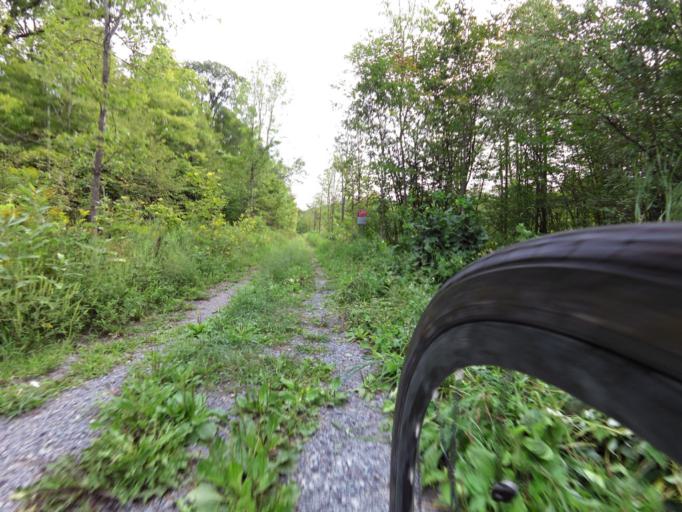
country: CA
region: Ontario
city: Gananoque
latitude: 44.6017
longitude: -76.2936
